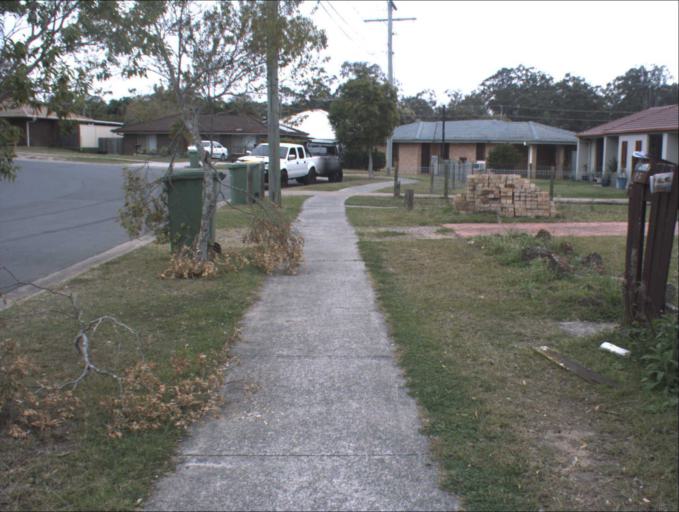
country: AU
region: Queensland
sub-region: Logan
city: Park Ridge South
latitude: -27.6724
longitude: 153.0467
